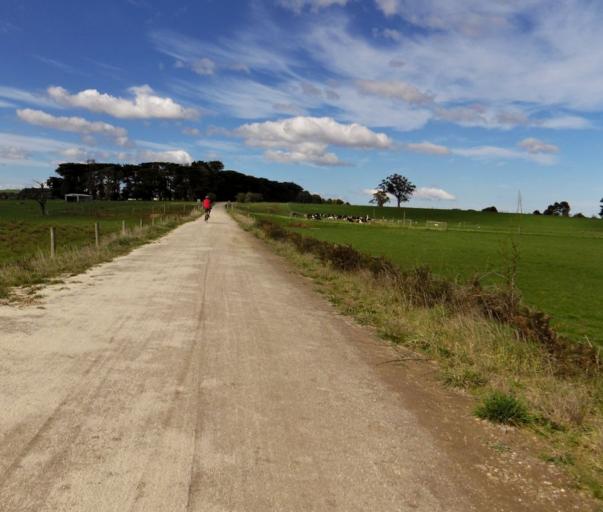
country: AU
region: Victoria
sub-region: Bass Coast
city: North Wonthaggi
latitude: -38.5225
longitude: 145.9438
